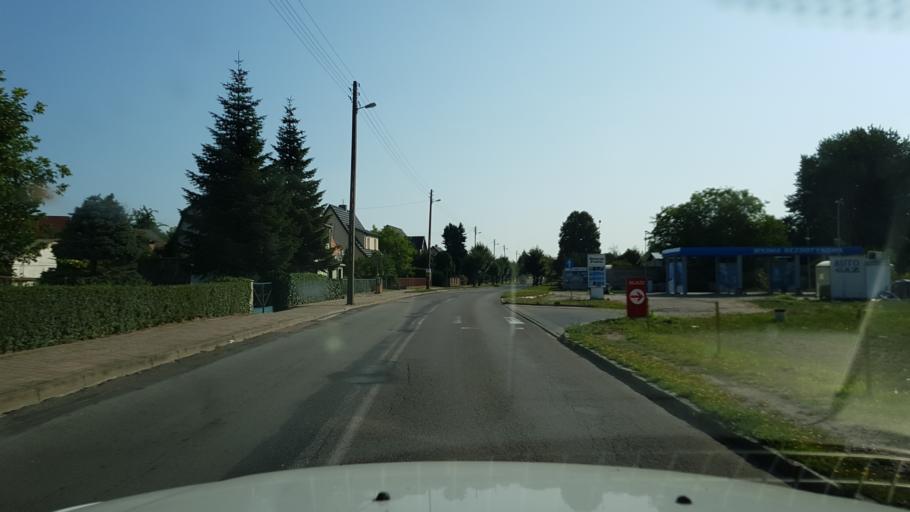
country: PL
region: West Pomeranian Voivodeship
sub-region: Powiat lobeski
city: Resko
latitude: 53.7740
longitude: 15.4157
